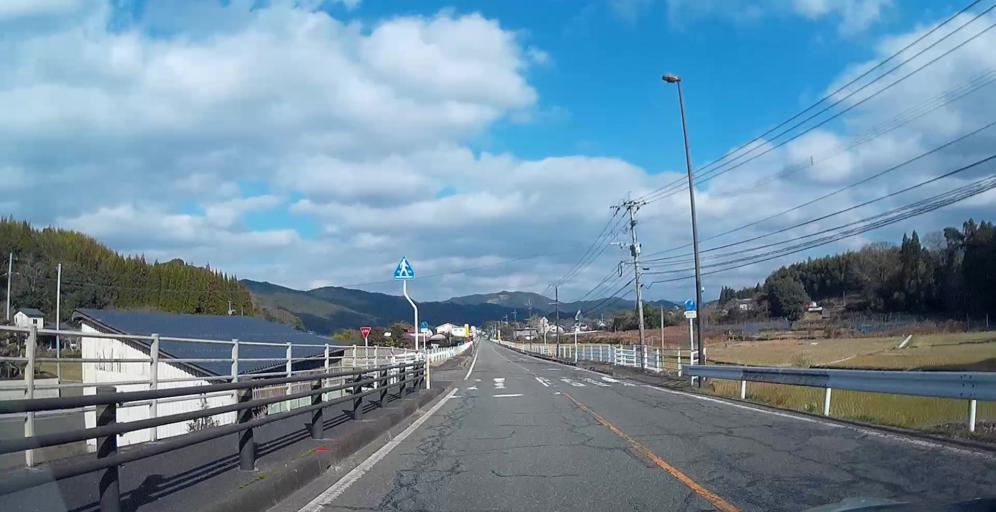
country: JP
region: Kumamoto
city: Yatsushiro
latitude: 32.3958
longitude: 130.5479
